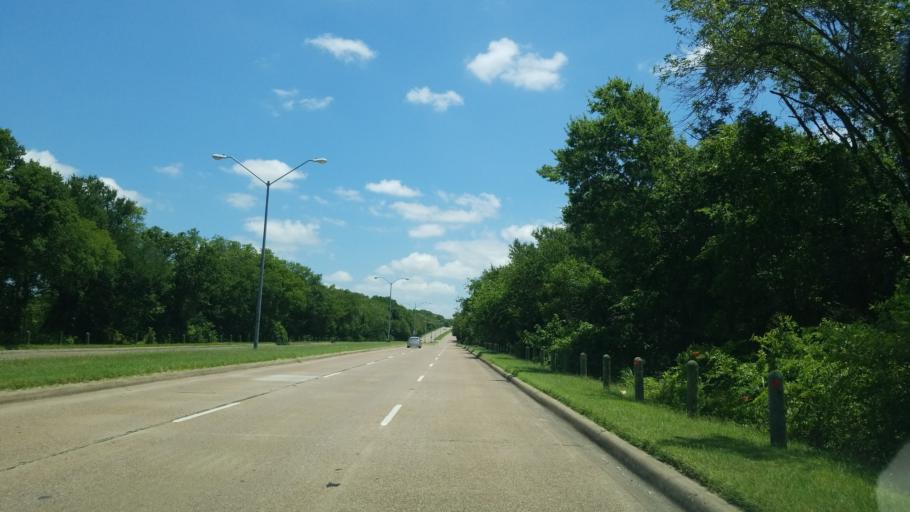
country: US
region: Texas
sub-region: Dallas County
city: Balch Springs
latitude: 32.7492
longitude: -96.7116
